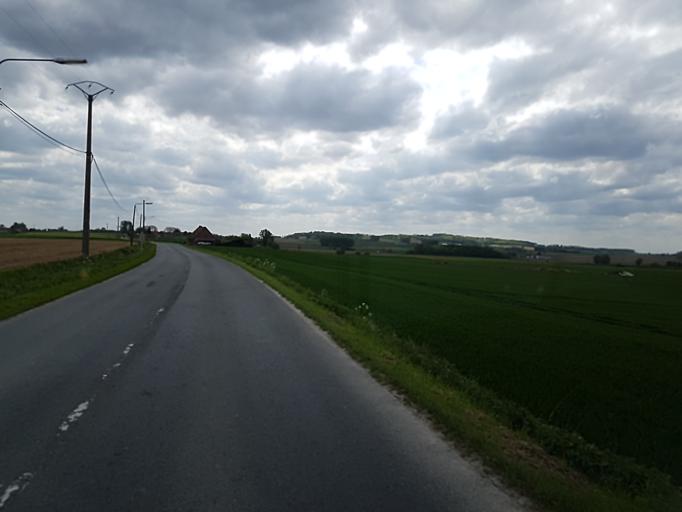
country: BE
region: Wallonia
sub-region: Province du Hainaut
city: Celles
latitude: 50.6787
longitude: 3.4521
